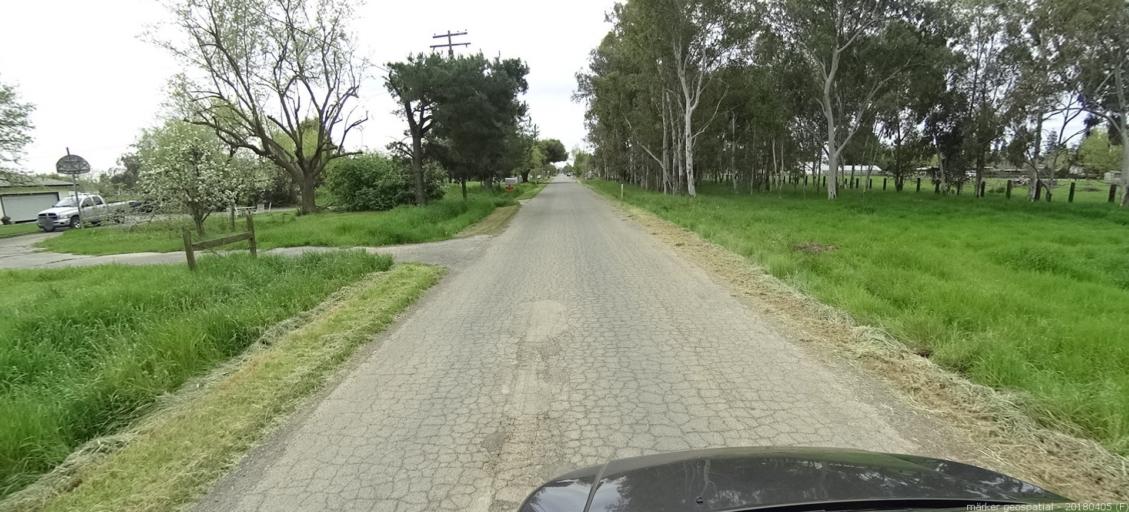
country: US
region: California
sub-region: Sacramento County
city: Galt
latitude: 38.2701
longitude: -121.3261
